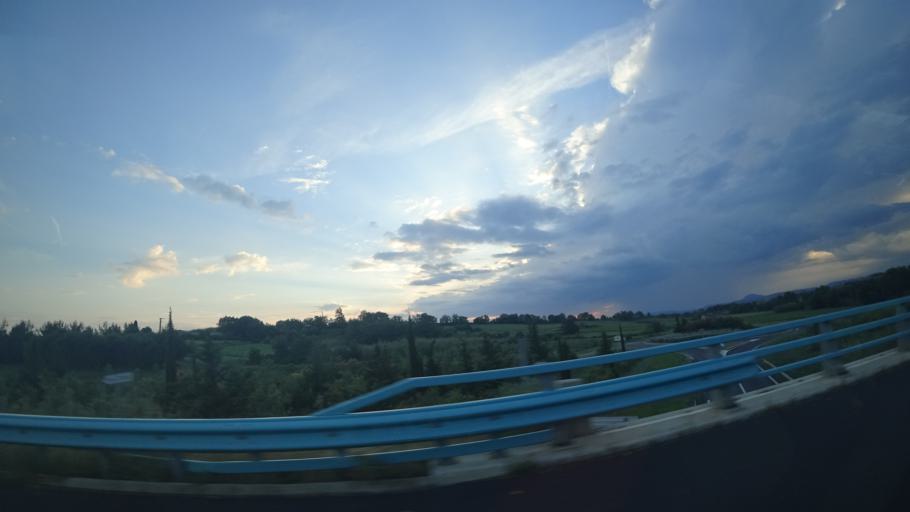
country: FR
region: Languedoc-Roussillon
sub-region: Departement de l'Herault
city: Paulhan
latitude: 43.5237
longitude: 3.4434
